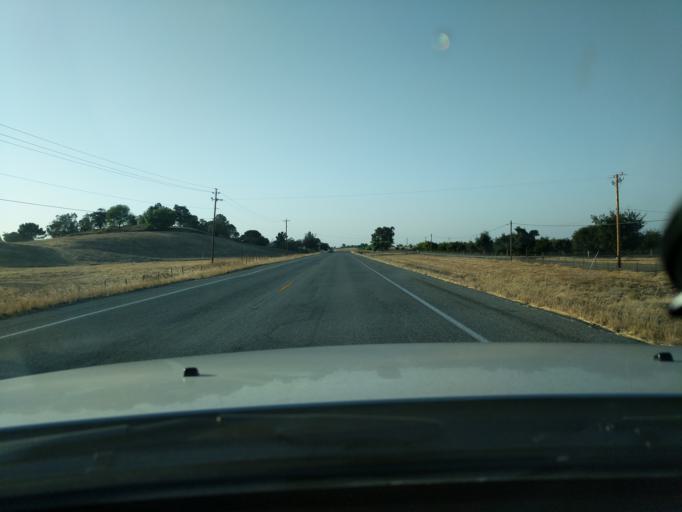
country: US
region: California
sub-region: San Benito County
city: Ridgemark
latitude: 36.8061
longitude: -121.3425
